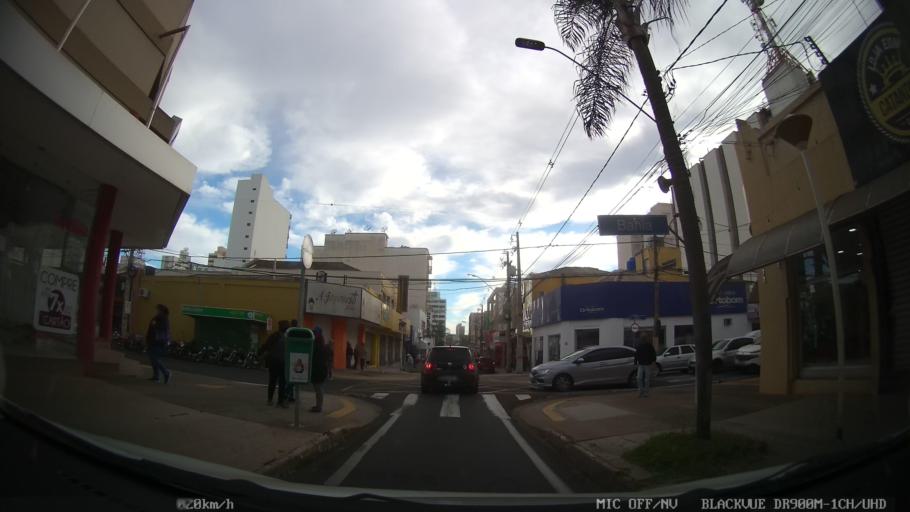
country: BR
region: Sao Paulo
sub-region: Catanduva
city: Catanduva
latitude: -21.1369
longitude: -48.9728
